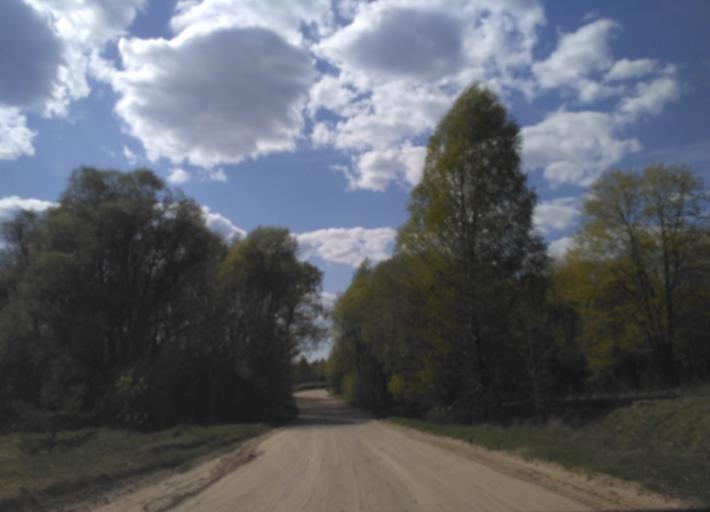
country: BY
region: Minsk
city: Narach
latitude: 54.9835
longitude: 26.6134
